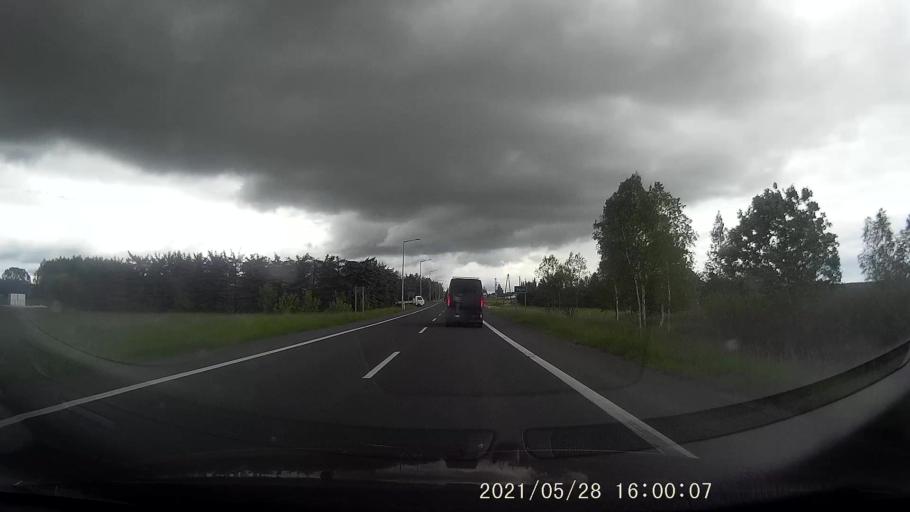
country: PL
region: Lower Silesian Voivodeship
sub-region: Powiat zgorzelecki
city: Lagow
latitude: 51.1536
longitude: 15.0878
